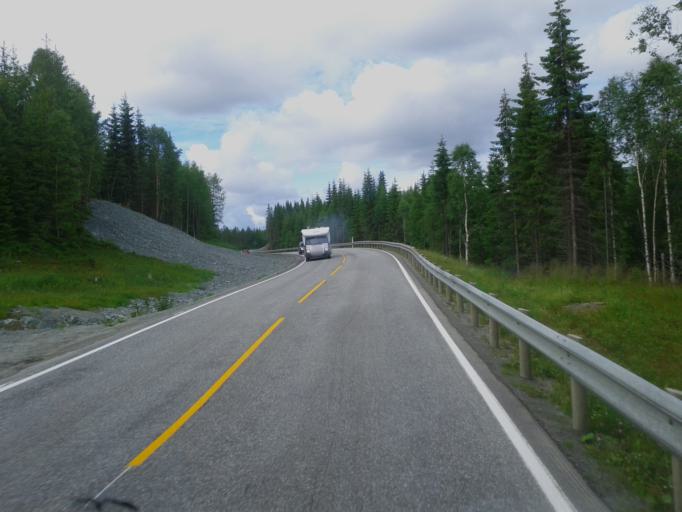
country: NO
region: Nord-Trondelag
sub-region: Hoylandet
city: Hoylandet
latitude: 64.6641
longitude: 12.6674
